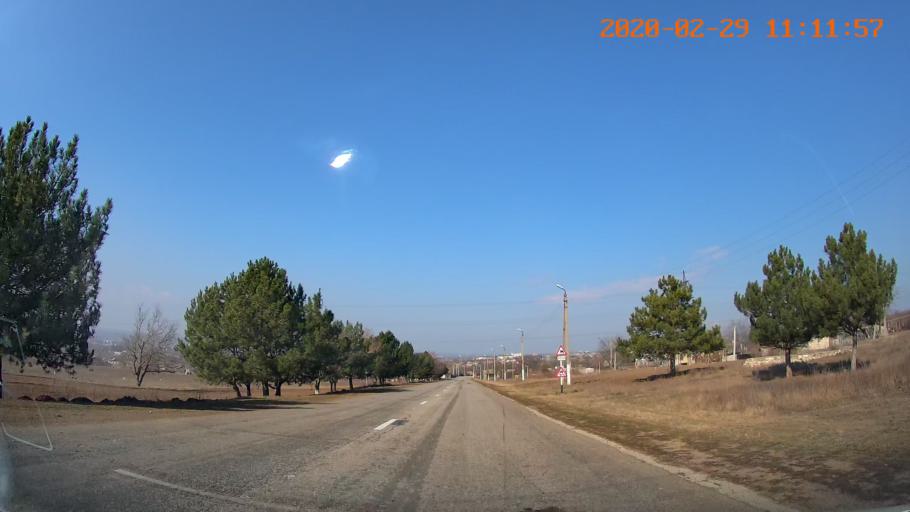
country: MD
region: Telenesti
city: Dubasari
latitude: 47.2589
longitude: 29.1909
